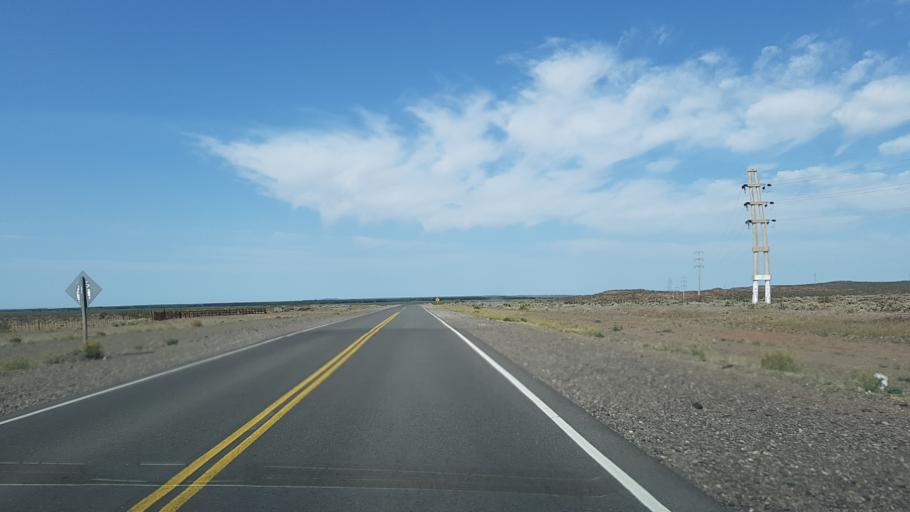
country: AR
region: Neuquen
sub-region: Departamento de Picun Leufu
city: Picun Leufu
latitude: -39.4558
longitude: -69.2384
